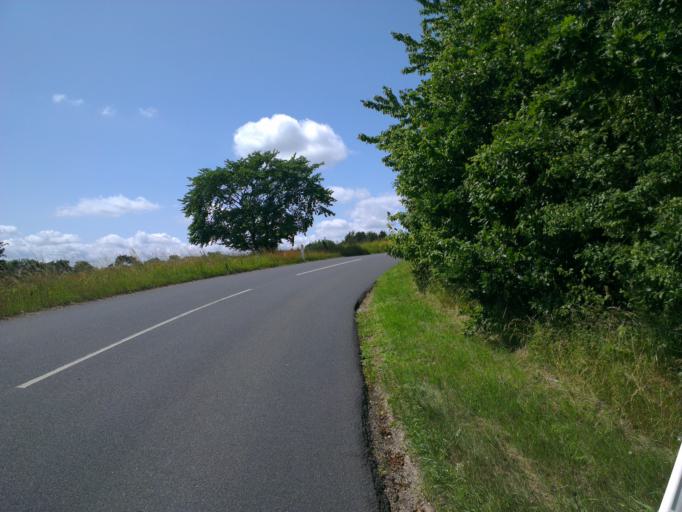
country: DK
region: Capital Region
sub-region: Frederikssund Kommune
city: Skibby
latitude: 55.7668
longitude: 11.9035
